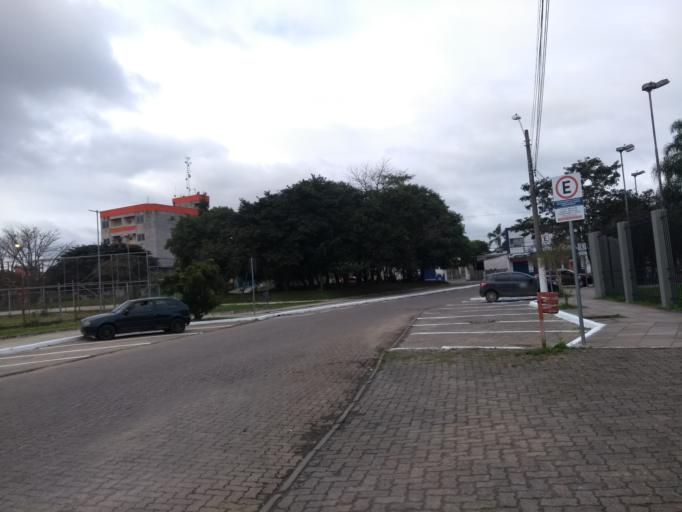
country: BR
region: Rio Grande do Sul
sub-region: Cachoeirinha
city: Cachoeirinha
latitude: -30.0007
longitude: -51.0762
